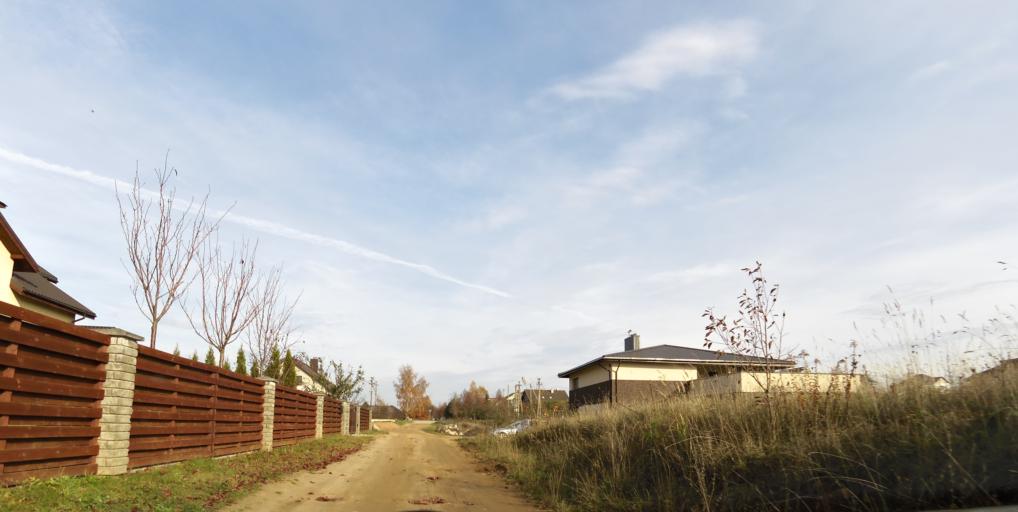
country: LT
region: Vilnius County
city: Pilaite
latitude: 54.7262
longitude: 25.1691
